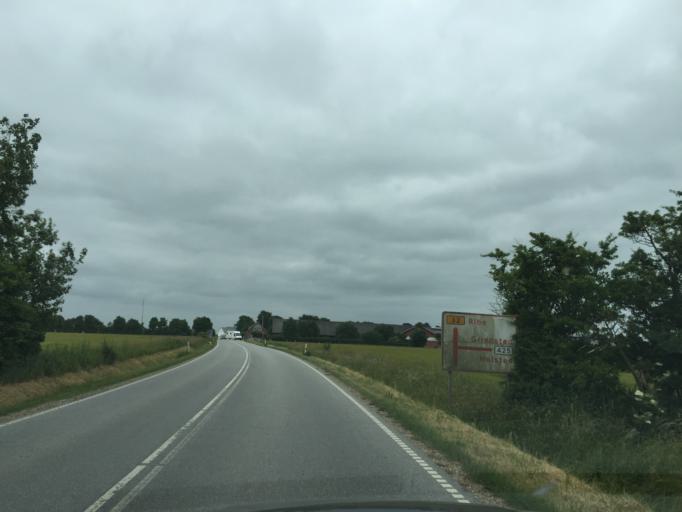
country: DK
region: South Denmark
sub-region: Vejen Kommune
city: Holsted
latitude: 55.3901
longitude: 8.8842
